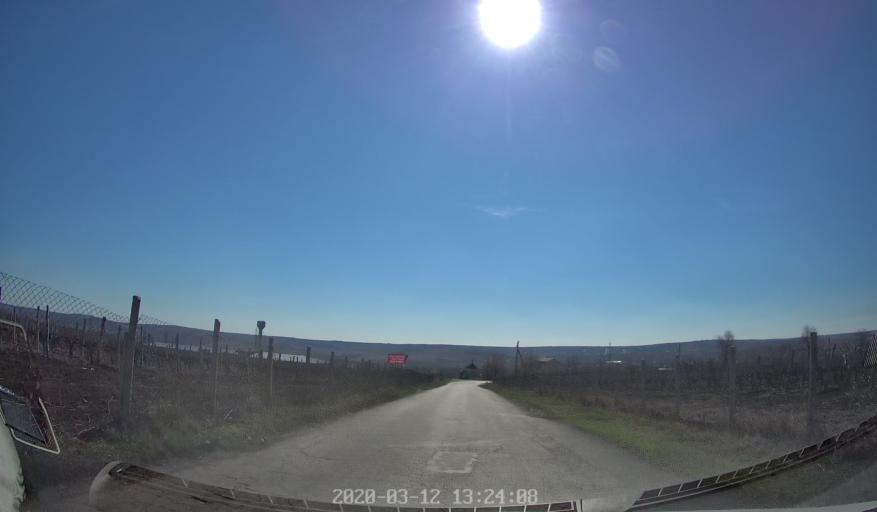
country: MD
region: Laloveni
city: Ialoveni
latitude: 46.9406
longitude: 28.8313
